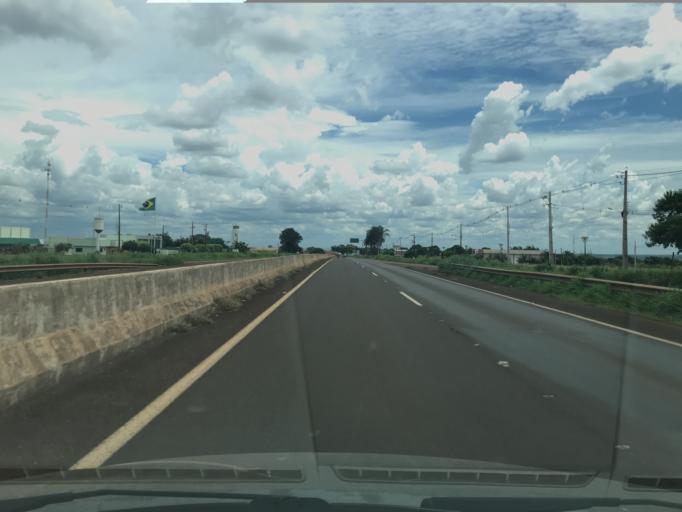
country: BR
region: Parana
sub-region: Paicandu
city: Paicandu
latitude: -23.4651
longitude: -52.0500
